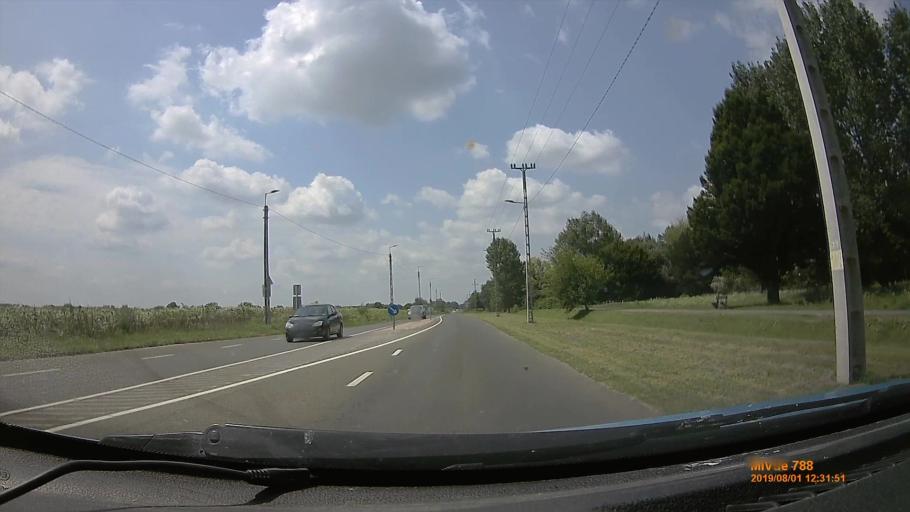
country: HU
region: Baranya
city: Siklos
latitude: 45.8577
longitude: 18.2747
